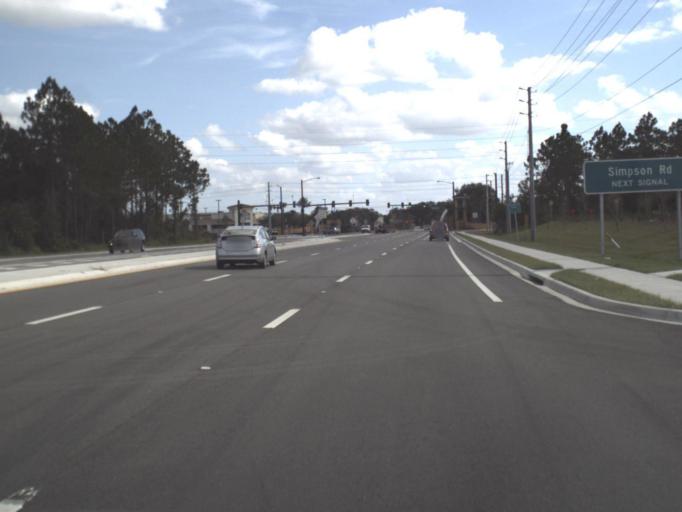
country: US
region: Florida
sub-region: Osceola County
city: Buenaventura Lakes
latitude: 28.3432
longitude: -81.3284
